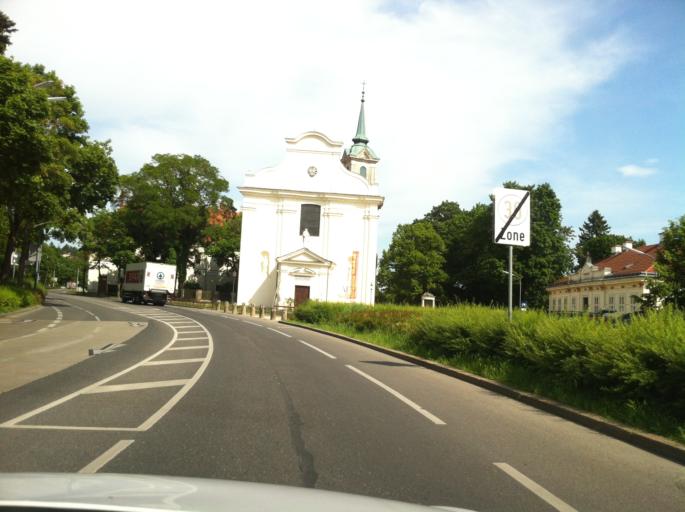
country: AT
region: Lower Austria
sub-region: Politischer Bezirk Wien-Umgebung
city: Purkersdorf
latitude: 48.2074
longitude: 16.2266
